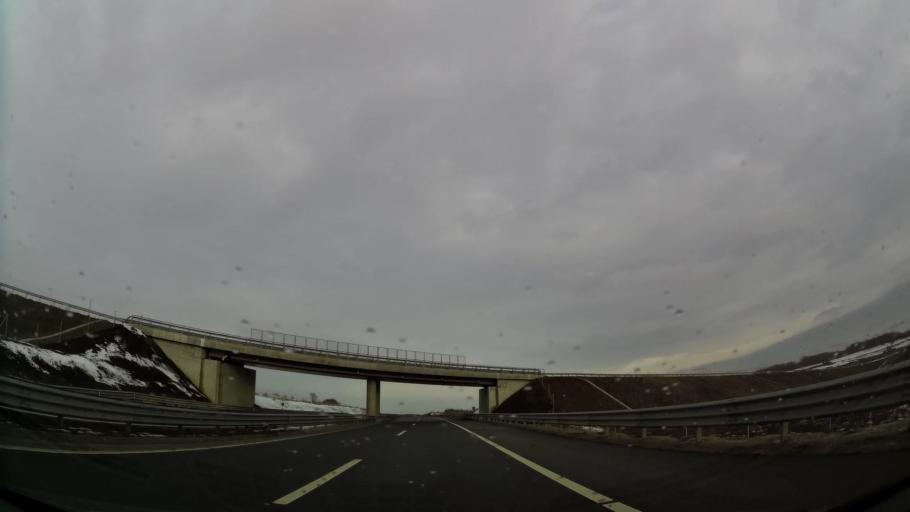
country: XK
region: Ferizaj
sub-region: Komuna e Ferizajt
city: Ferizaj
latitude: 42.3496
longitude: 21.2053
